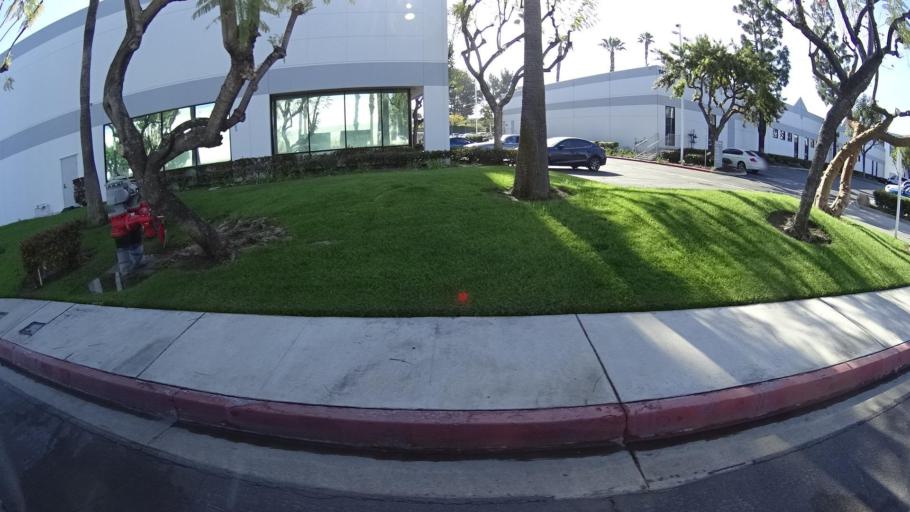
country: US
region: California
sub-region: Los Angeles County
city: South San Jose Hills
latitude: 33.9959
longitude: -117.8953
